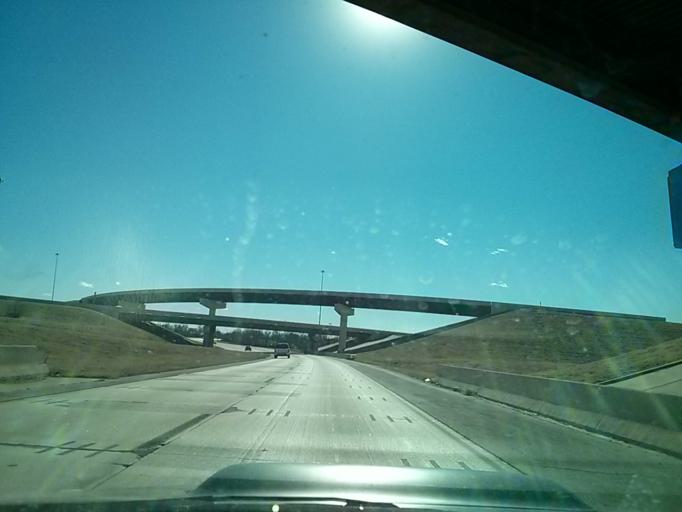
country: US
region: Oklahoma
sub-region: Tulsa County
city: Turley
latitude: 36.2002
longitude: -95.9502
